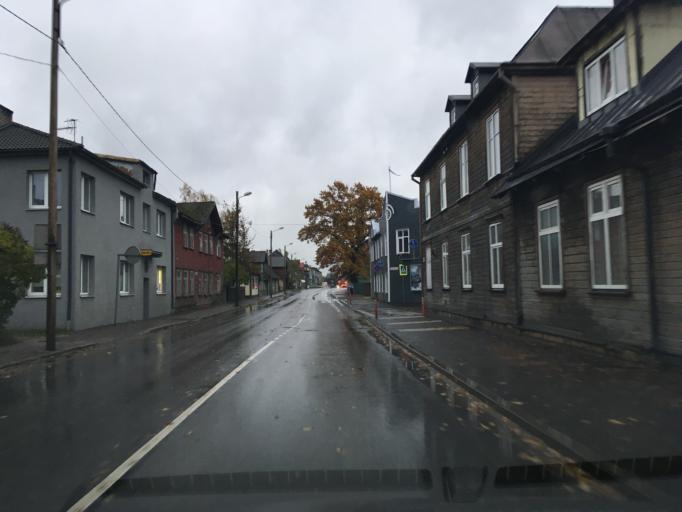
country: EE
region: Paernumaa
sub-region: Paernu linn
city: Parnu
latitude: 58.3947
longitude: 24.4942
